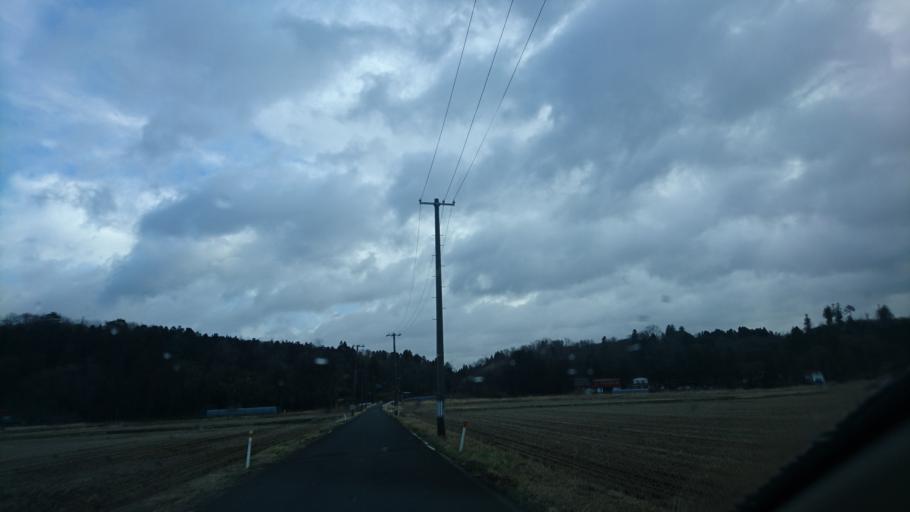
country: JP
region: Iwate
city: Ichinoseki
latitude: 38.7843
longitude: 141.0365
